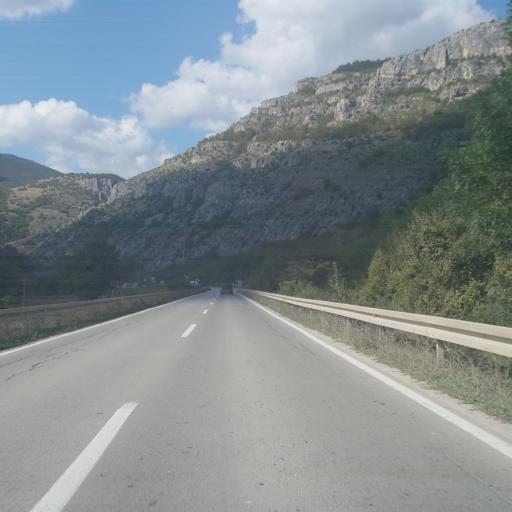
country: RS
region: Central Serbia
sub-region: Nisavski Okrug
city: Svrljig
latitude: 43.3075
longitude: 22.1880
